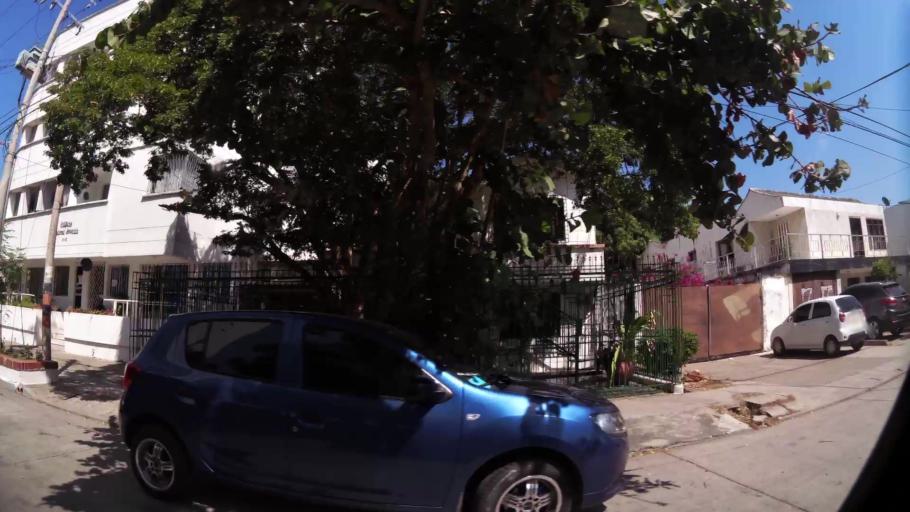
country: CO
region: Bolivar
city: Cartagena
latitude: 10.4446
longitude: -75.5190
